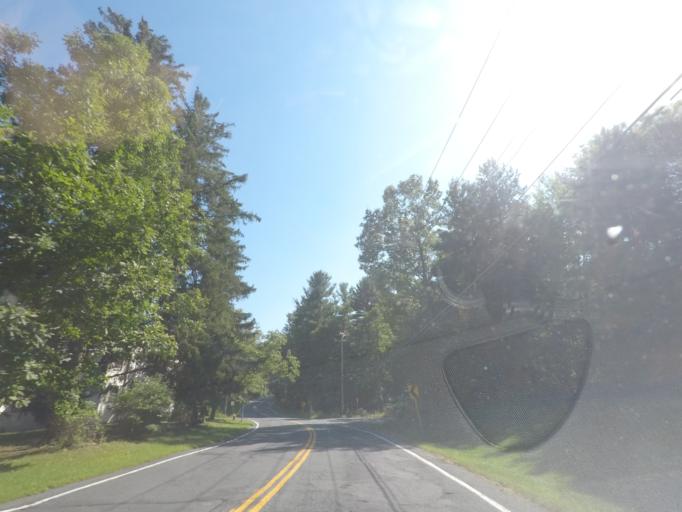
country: US
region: New York
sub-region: Albany County
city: Menands
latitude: 42.7106
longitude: -73.7430
